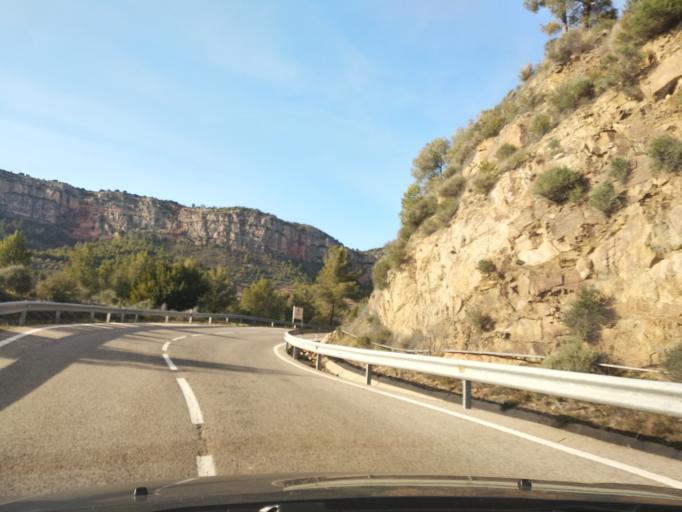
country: ES
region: Catalonia
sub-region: Provincia de Tarragona
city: Margalef
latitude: 41.2371
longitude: 0.7850
